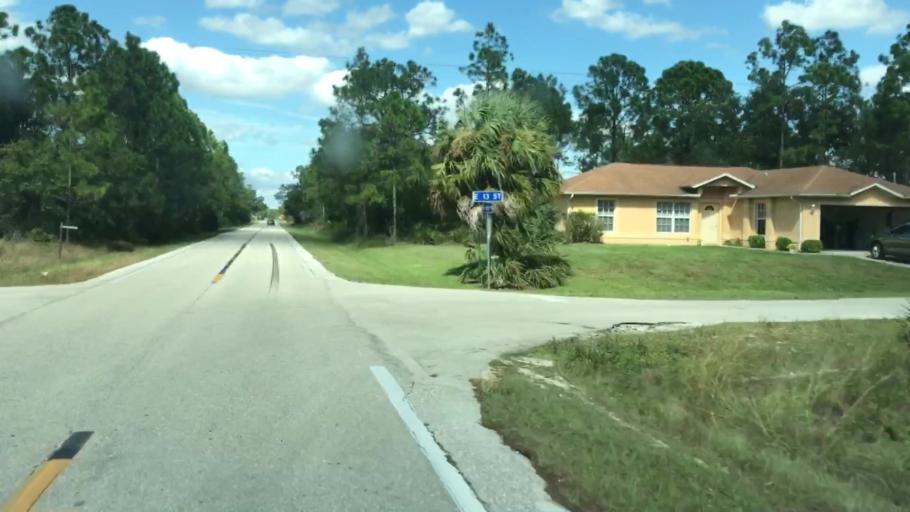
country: US
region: Florida
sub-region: Lee County
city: Lehigh Acres
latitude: 26.6473
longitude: -81.6256
